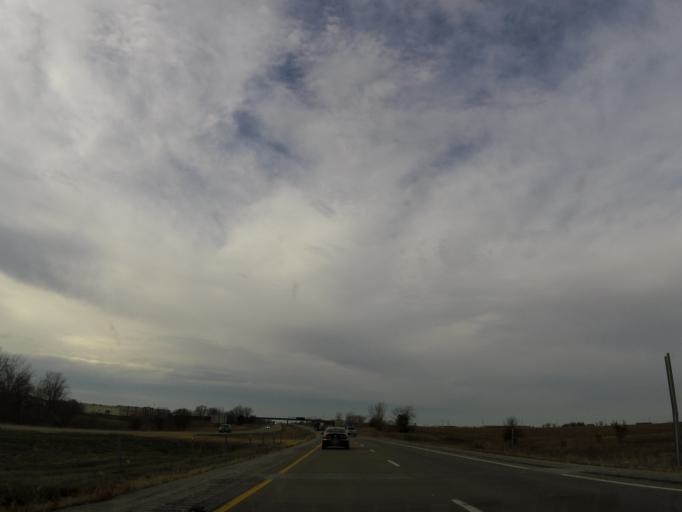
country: US
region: Iowa
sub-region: Scott County
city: Eldridge
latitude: 41.5996
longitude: -90.5911
